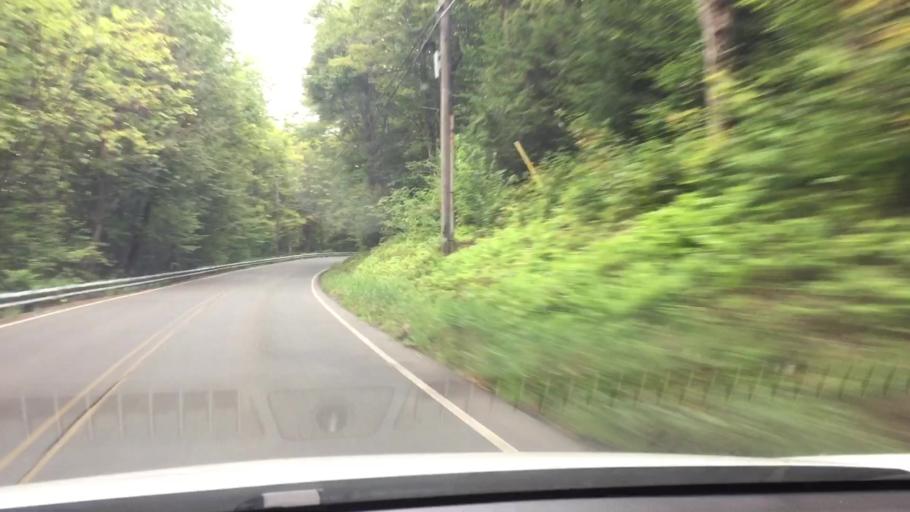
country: US
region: Massachusetts
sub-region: Berkshire County
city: Otis
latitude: 42.2212
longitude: -72.9580
